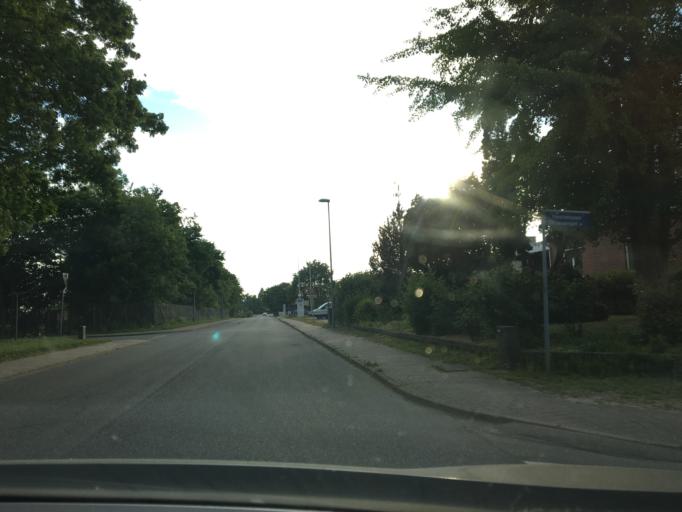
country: DK
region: South Denmark
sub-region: Fredericia Kommune
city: Fredericia
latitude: 55.5813
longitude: 9.7727
